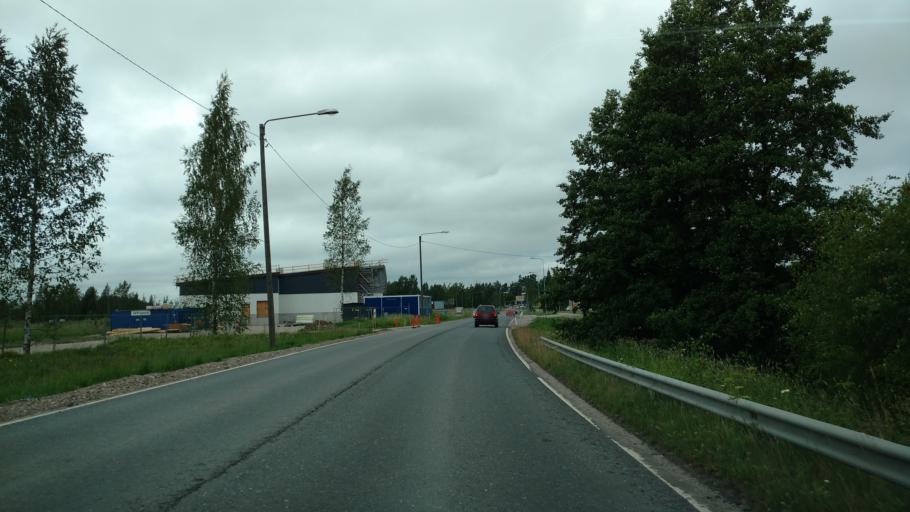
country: FI
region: Varsinais-Suomi
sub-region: Salo
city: Halikko
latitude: 60.3953
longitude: 23.0848
